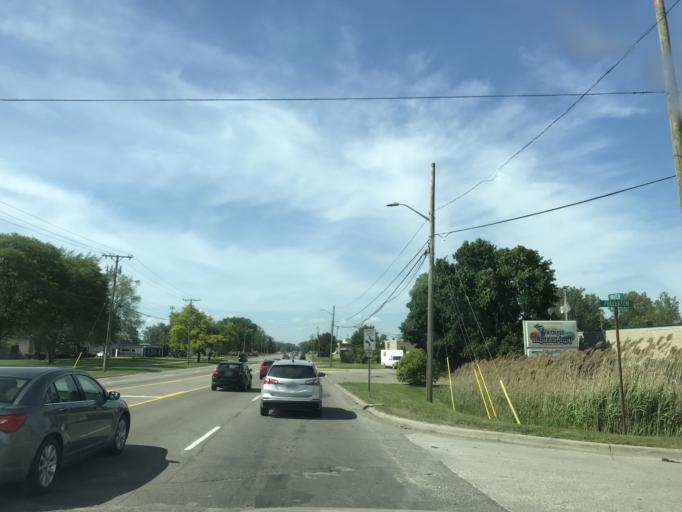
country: US
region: Michigan
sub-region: Wayne County
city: Redford
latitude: 42.3773
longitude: -83.3138
